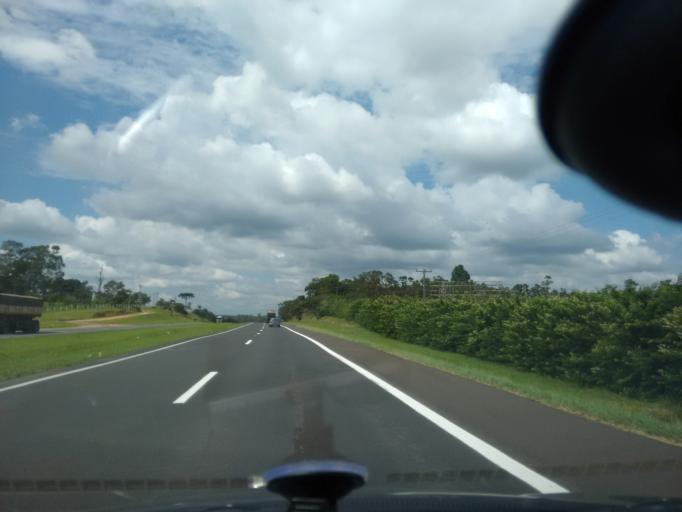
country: BR
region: Sao Paulo
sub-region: Sao Carlos
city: Sao Carlos
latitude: -22.0808
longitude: -47.8392
